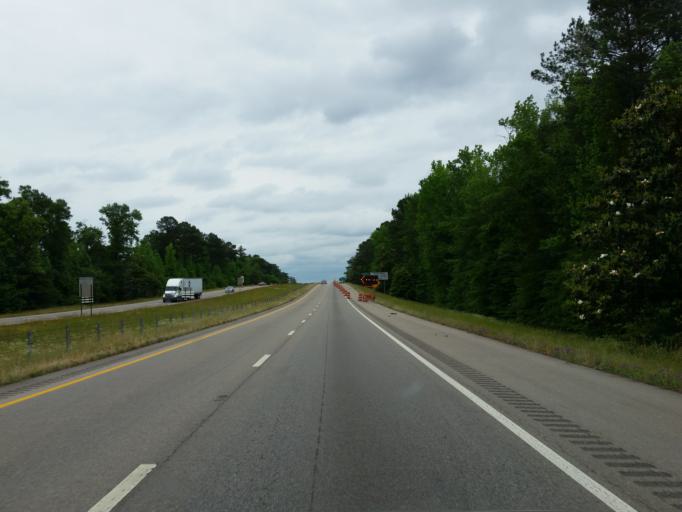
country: US
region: Alabama
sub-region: Sumter County
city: York
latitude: 32.4180
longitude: -88.4575
